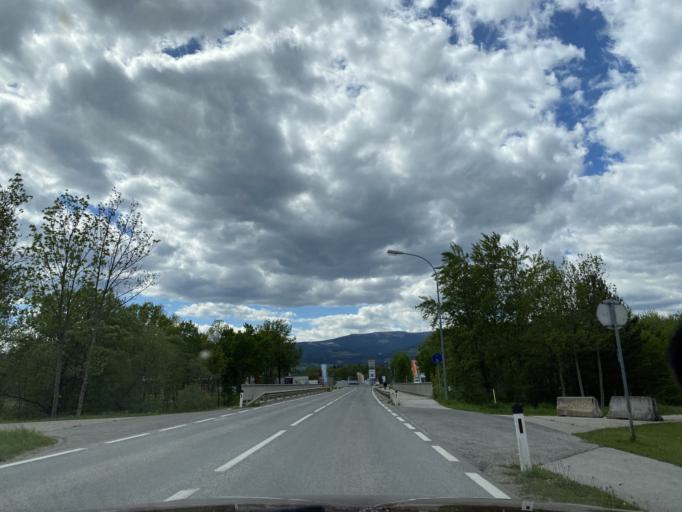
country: AT
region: Carinthia
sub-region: Politischer Bezirk Wolfsberg
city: Wolfsberg
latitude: 46.8186
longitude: 14.8418
